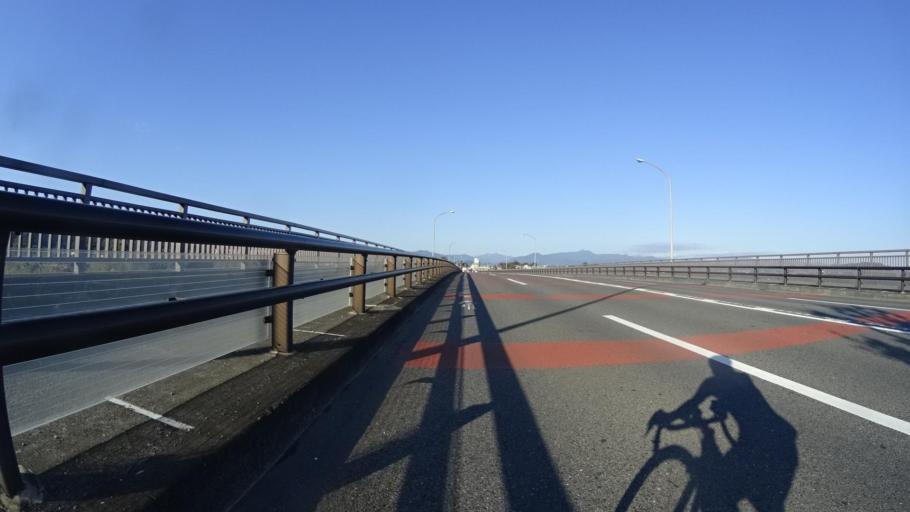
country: JP
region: Tokyo
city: Fussa
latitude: 35.7202
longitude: 139.3289
